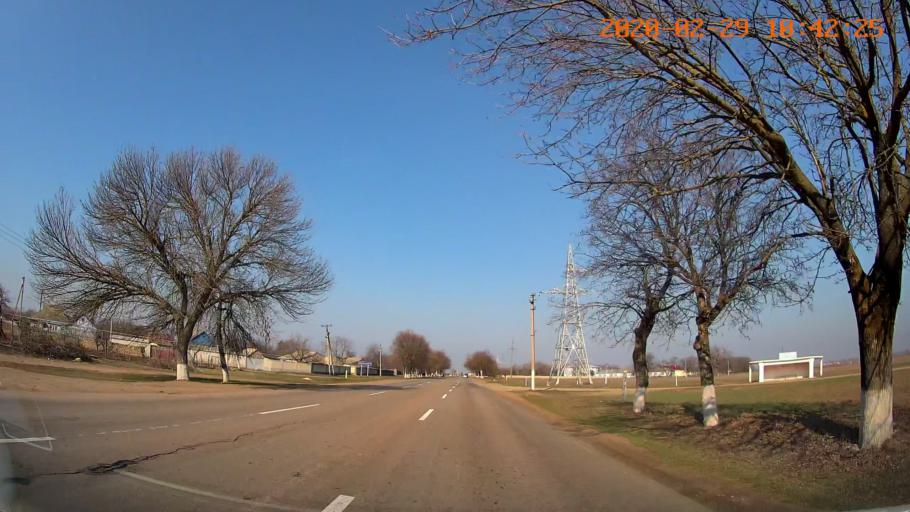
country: MD
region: Telenesti
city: Grigoriopol
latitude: 47.0514
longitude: 29.4113
